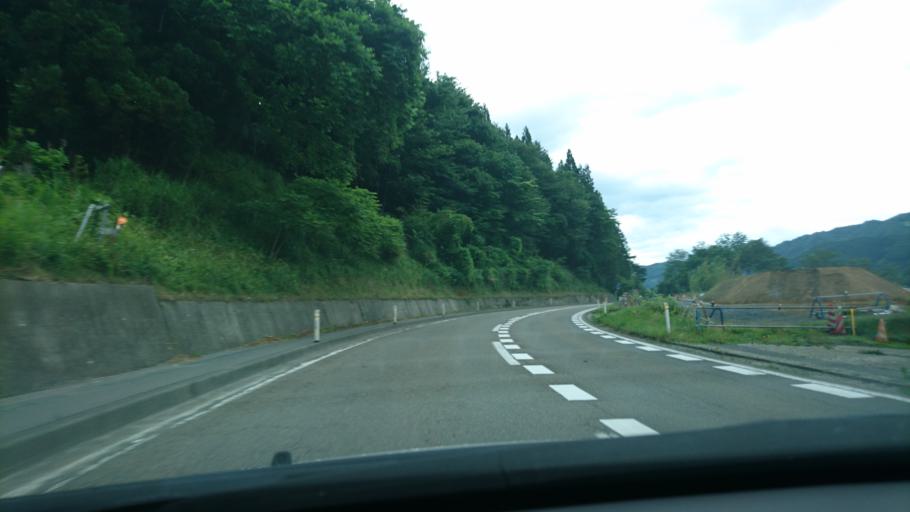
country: JP
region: Iwate
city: Kamaishi
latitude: 39.2111
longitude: 141.8664
